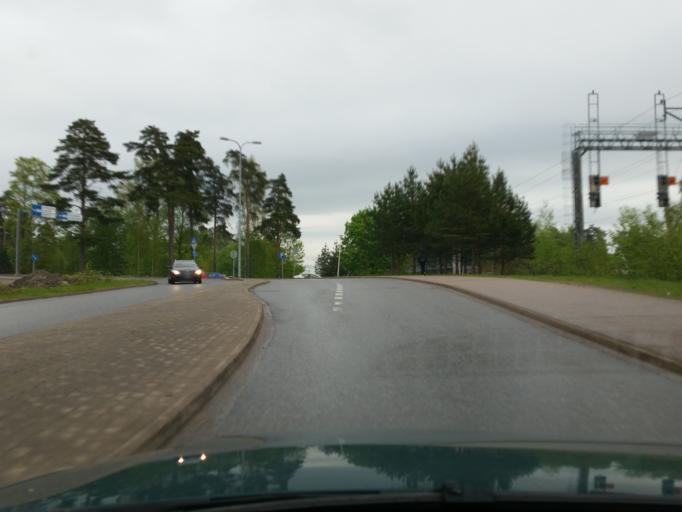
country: FI
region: Uusimaa
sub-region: Helsinki
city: Teekkarikylae
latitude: 60.2199
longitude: 24.8384
